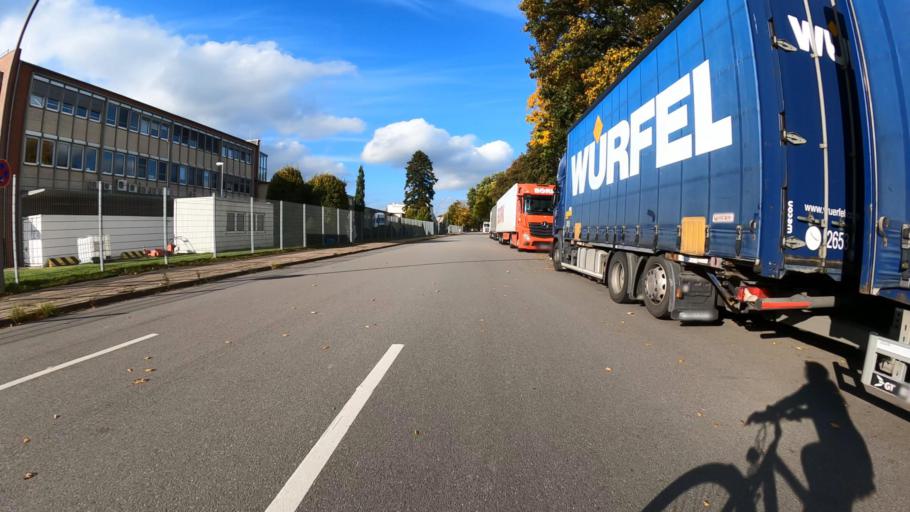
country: DE
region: Schleswig-Holstein
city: Delingsdorf
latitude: 53.6809
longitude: 10.2537
